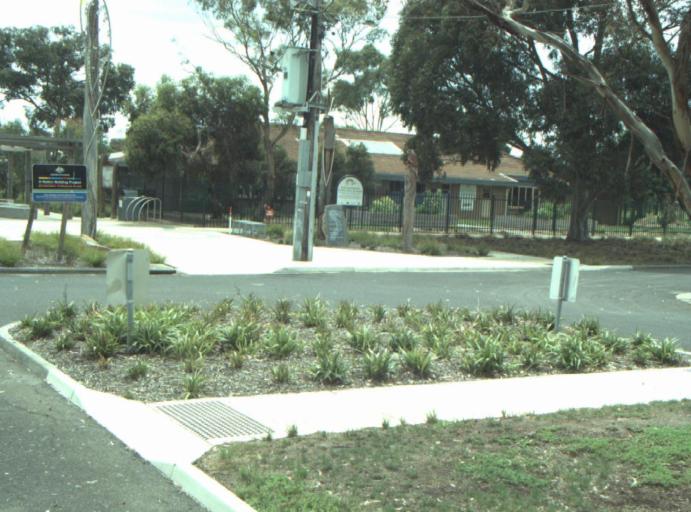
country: AU
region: Victoria
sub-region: Greater Geelong
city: Breakwater
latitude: -38.1798
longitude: 144.3949
